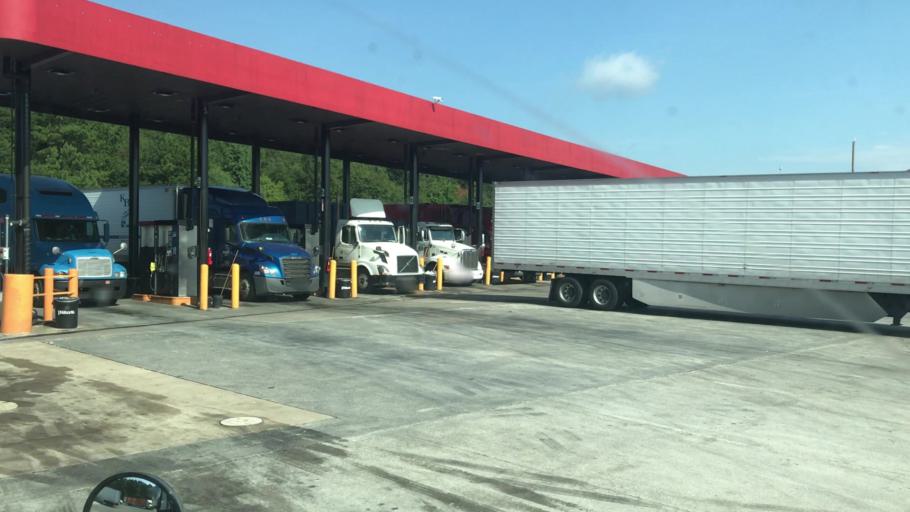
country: US
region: Georgia
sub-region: Bartow County
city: Cartersville
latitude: 34.2717
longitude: -84.8073
